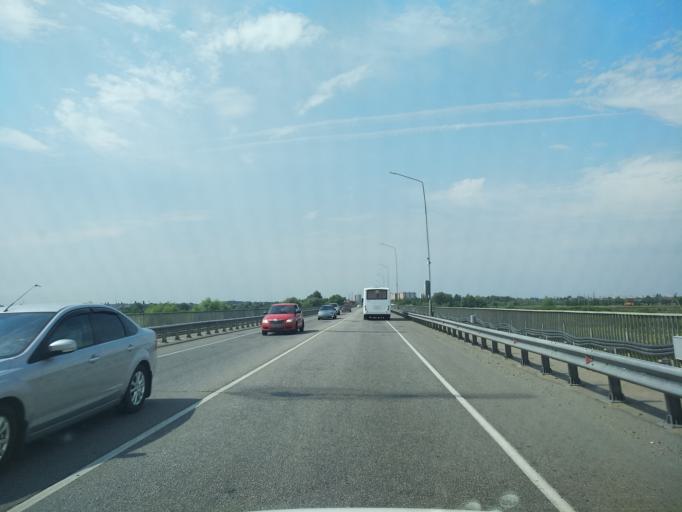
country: RU
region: Voronezj
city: Somovo
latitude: 51.6849
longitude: 39.3507
